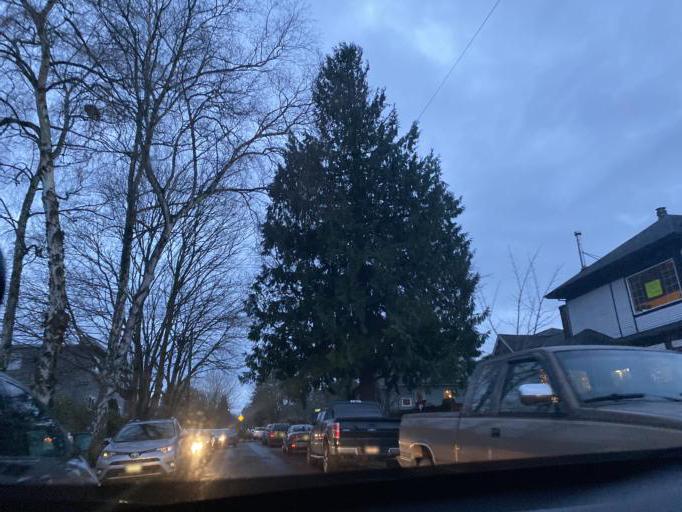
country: US
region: Washington
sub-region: King County
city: Seattle
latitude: 47.6385
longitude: -122.3636
